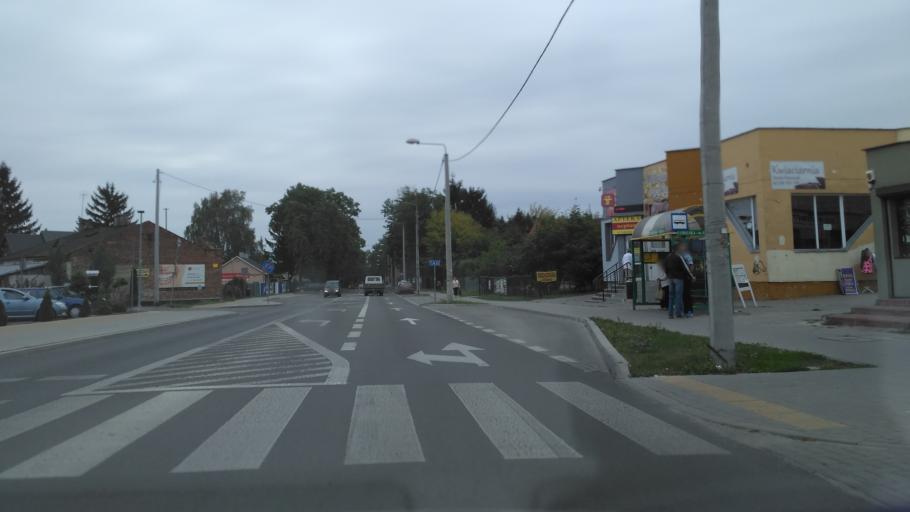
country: PL
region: Lublin Voivodeship
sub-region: Chelm
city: Chelm
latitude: 51.1458
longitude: 23.4382
